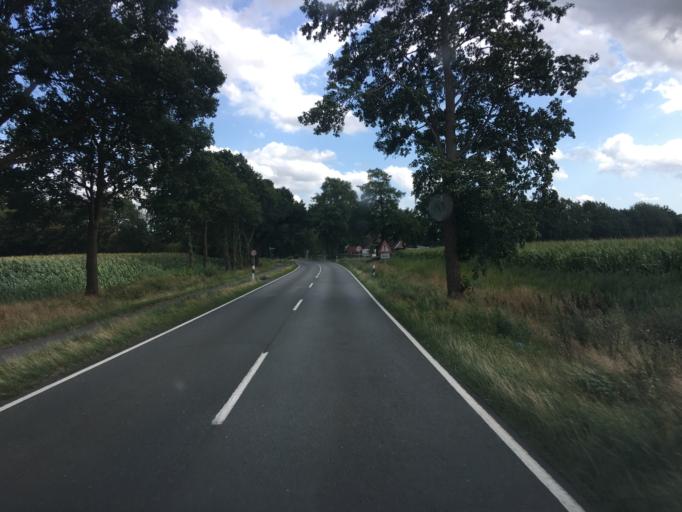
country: DE
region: Lower Saxony
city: Friesoythe
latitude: 53.0579
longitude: 7.8529
